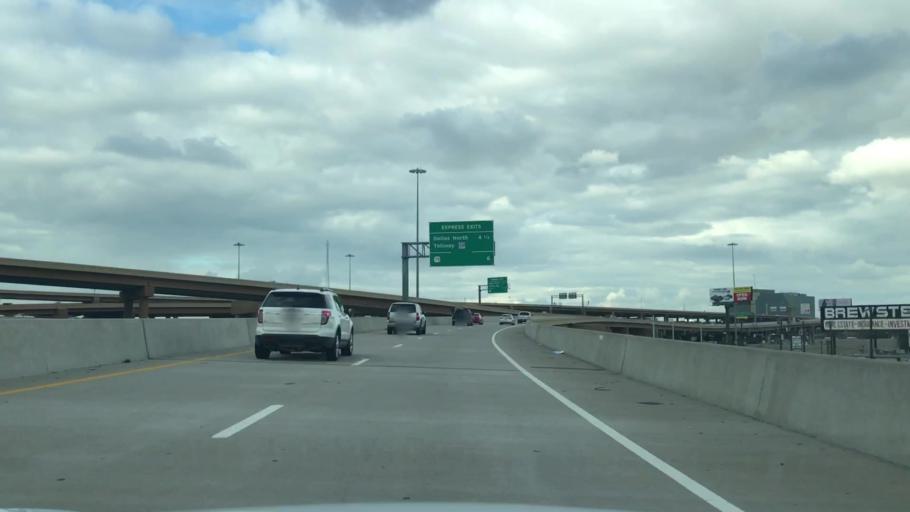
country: US
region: Texas
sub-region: Dallas County
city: Farmers Branch
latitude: 32.9060
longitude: -96.8961
